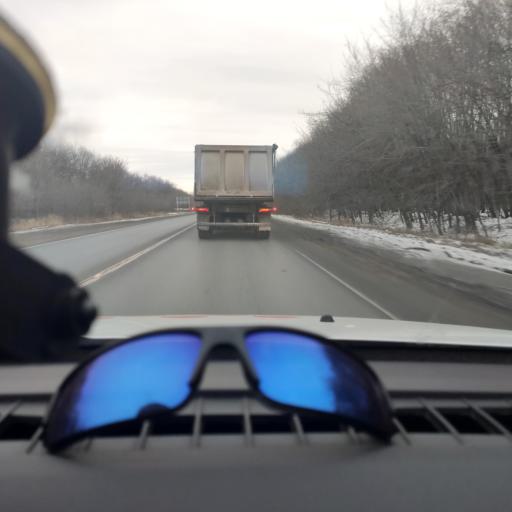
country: RU
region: Samara
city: Novokuybyshevsk
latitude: 52.9830
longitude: 49.8850
